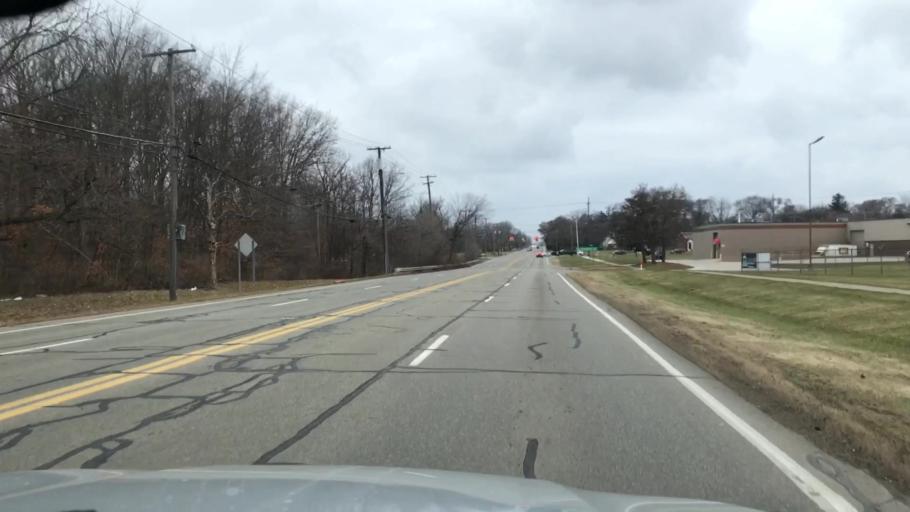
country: US
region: Michigan
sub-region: Wayne County
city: Westland
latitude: 42.3678
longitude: -83.4083
